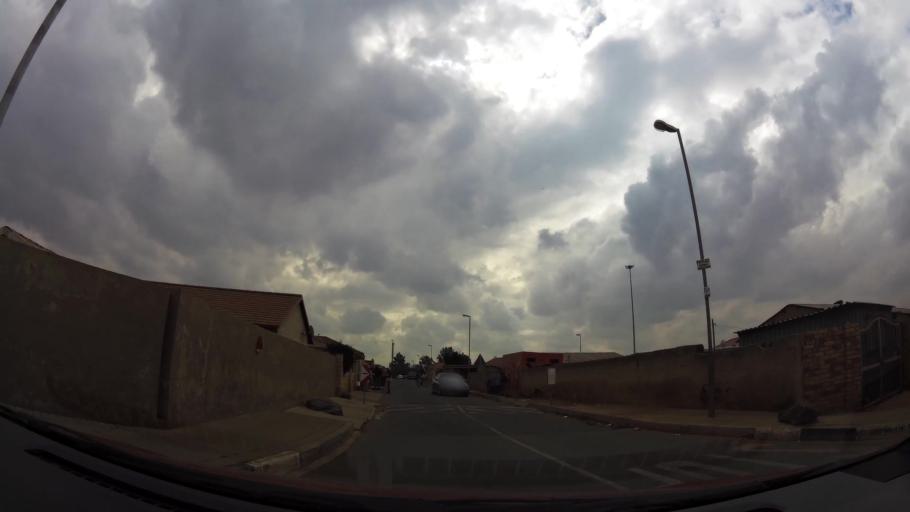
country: ZA
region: Gauteng
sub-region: City of Johannesburg Metropolitan Municipality
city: Soweto
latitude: -26.2653
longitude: 27.8350
